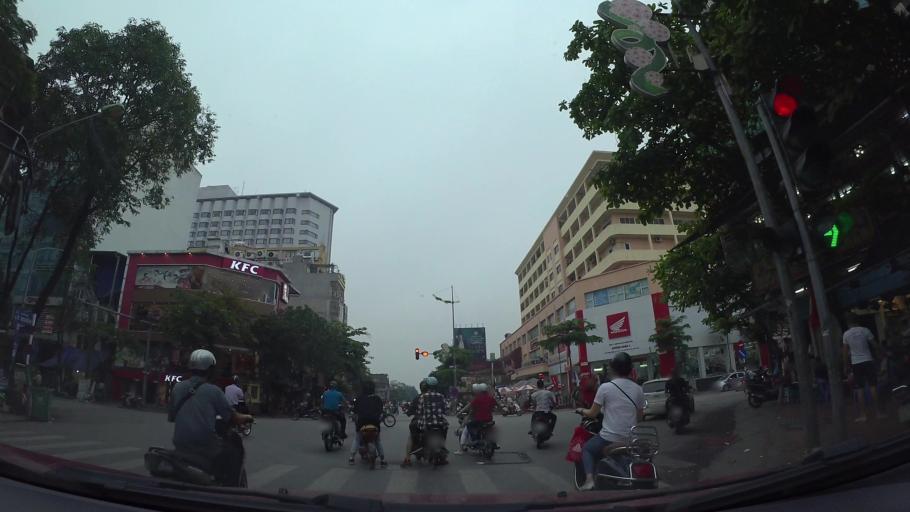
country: VN
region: Ha Noi
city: Hanoi
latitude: 21.0191
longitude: 105.8413
